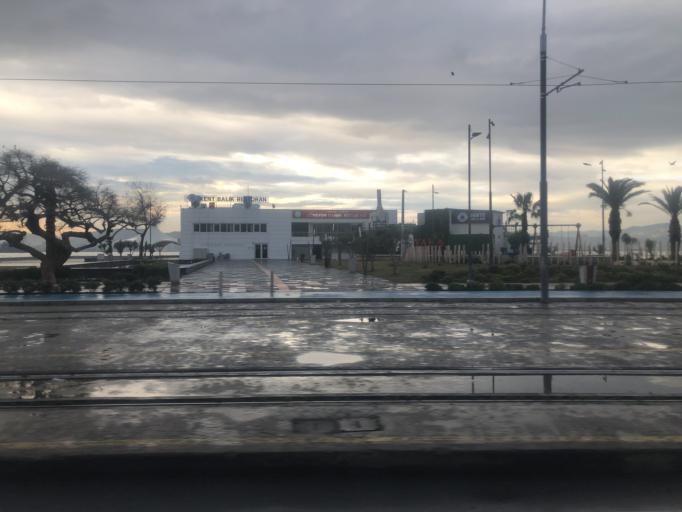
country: TR
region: Izmir
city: Karsiyaka
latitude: 38.4497
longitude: 27.1115
